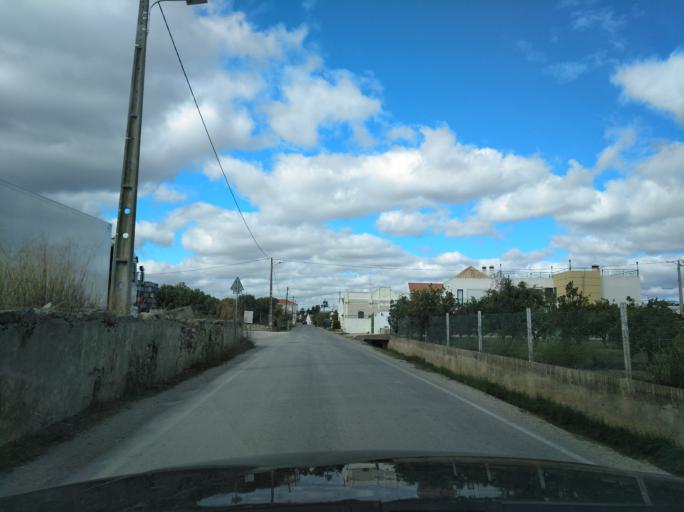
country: PT
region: Faro
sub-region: Tavira
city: Luz
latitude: 37.0956
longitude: -7.7049
